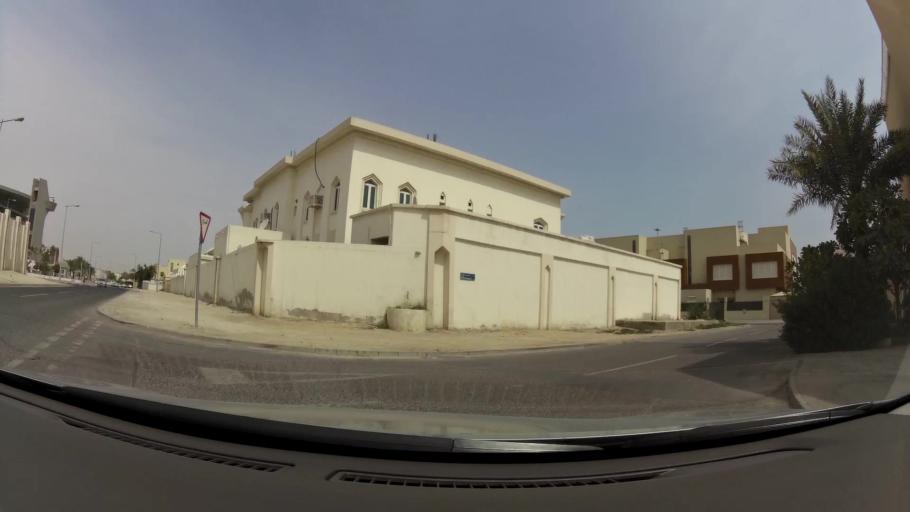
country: QA
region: Baladiyat ad Dawhah
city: Doha
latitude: 25.2692
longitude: 51.4920
